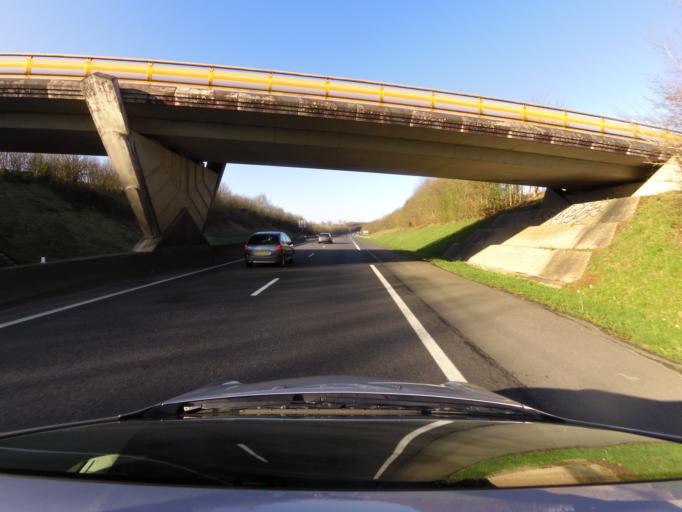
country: FR
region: Lower Normandy
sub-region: Departement du Calvados
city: Saint-Martin-des-Besaces
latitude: 49.0181
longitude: -0.8453
